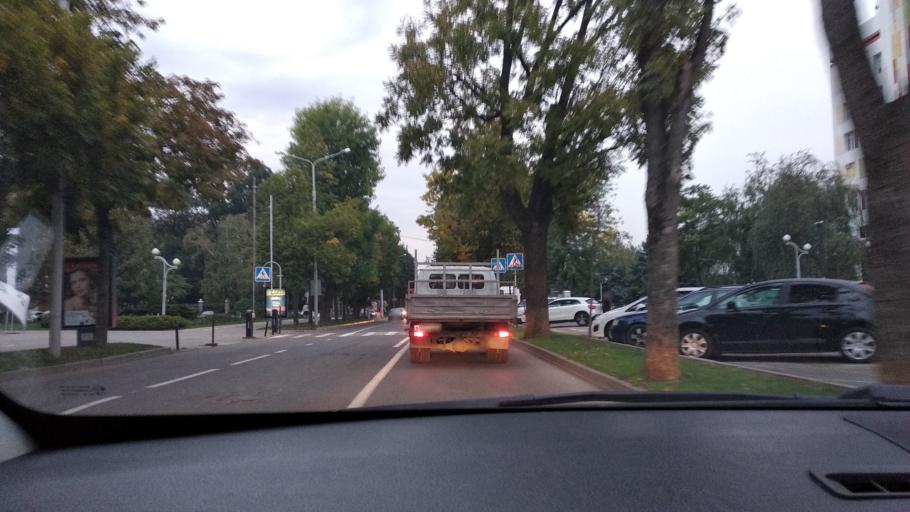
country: RU
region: Krasnodarskiy
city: Krasnodar
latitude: 45.0154
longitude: 38.9638
